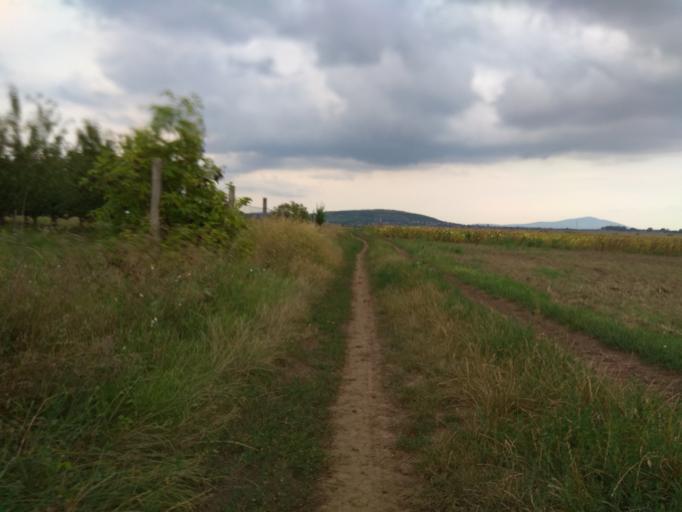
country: HU
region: Borsod-Abauj-Zemplen
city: Bekecs
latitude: 48.1509
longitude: 21.1166
